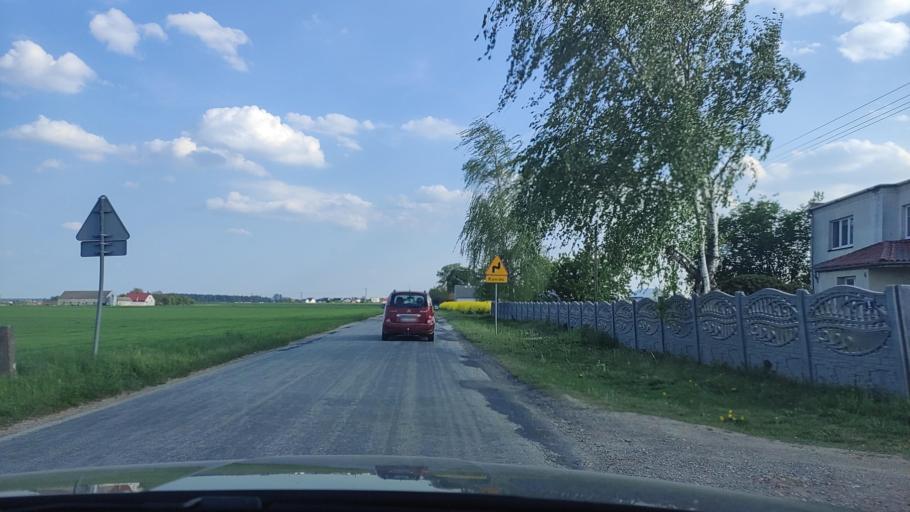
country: PL
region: Greater Poland Voivodeship
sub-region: Powiat poznanski
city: Kleszczewo
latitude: 52.3653
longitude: 17.1678
